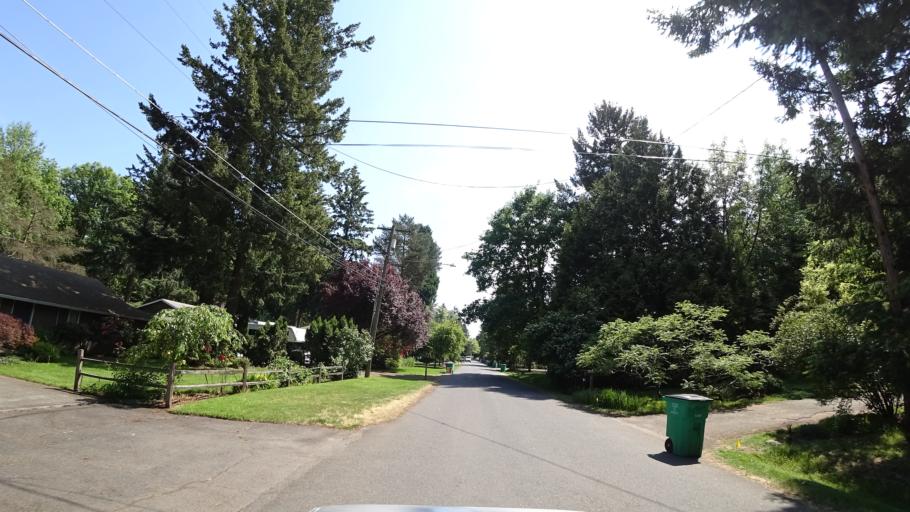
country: US
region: Oregon
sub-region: Washington County
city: Metzger
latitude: 45.4544
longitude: -122.7317
